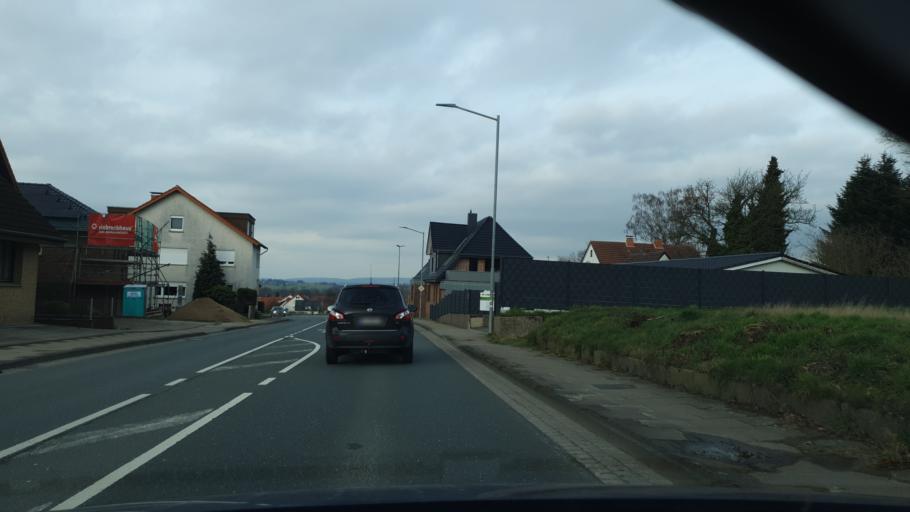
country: DE
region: North Rhine-Westphalia
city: Spenge
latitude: 52.1321
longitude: 8.4863
